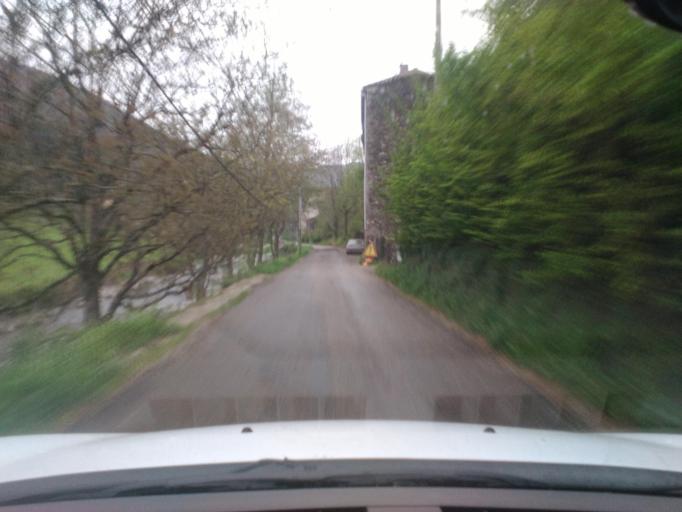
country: FR
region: Languedoc-Roussillon
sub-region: Departement du Gard
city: Valleraugue
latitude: 44.0923
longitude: 3.6359
